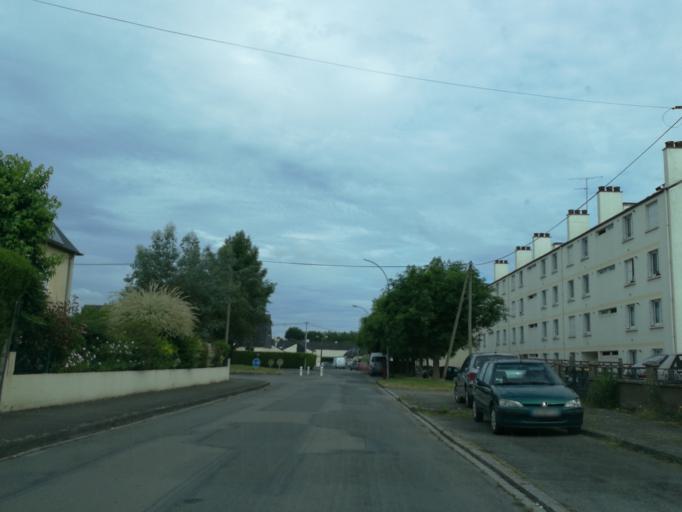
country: FR
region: Brittany
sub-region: Departement d'Ille-et-Vilaine
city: Montauban-de-Bretagne
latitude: 48.1948
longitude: -2.0461
